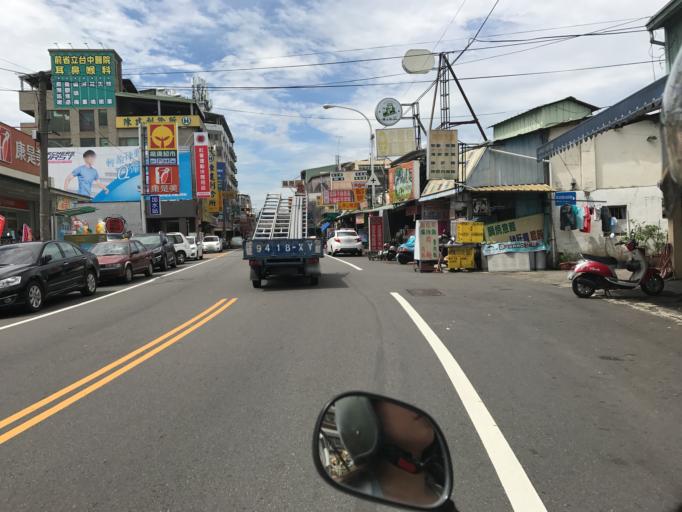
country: TW
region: Taiwan
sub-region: Taichung City
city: Taichung
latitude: 24.0874
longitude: 120.7025
